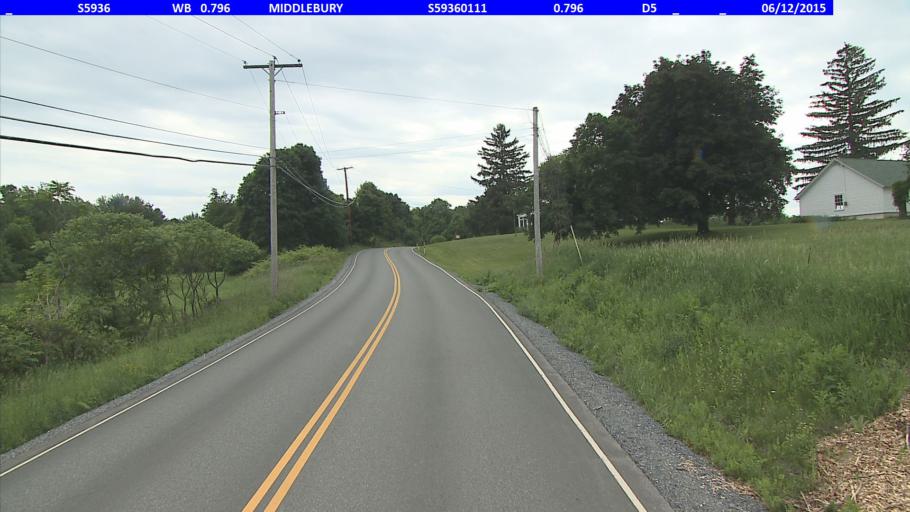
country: US
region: Vermont
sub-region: Addison County
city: Middlebury (village)
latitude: 44.0243
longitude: -73.1499
